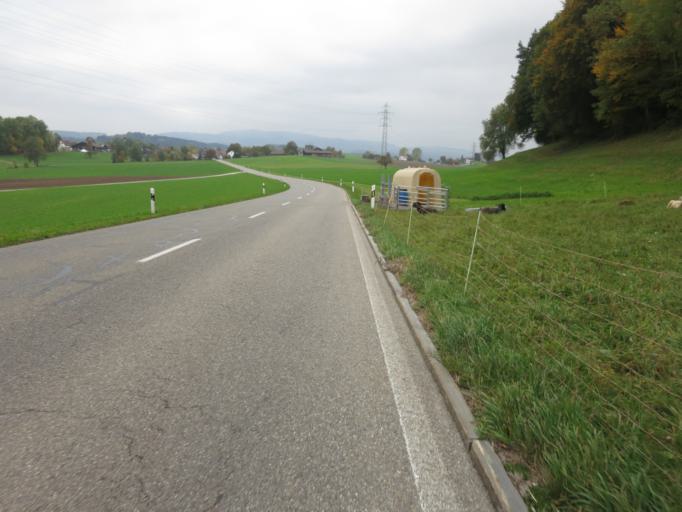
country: CH
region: Zurich
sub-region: Bezirk Hinwil
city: Binzikon
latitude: 47.2827
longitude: 8.7842
